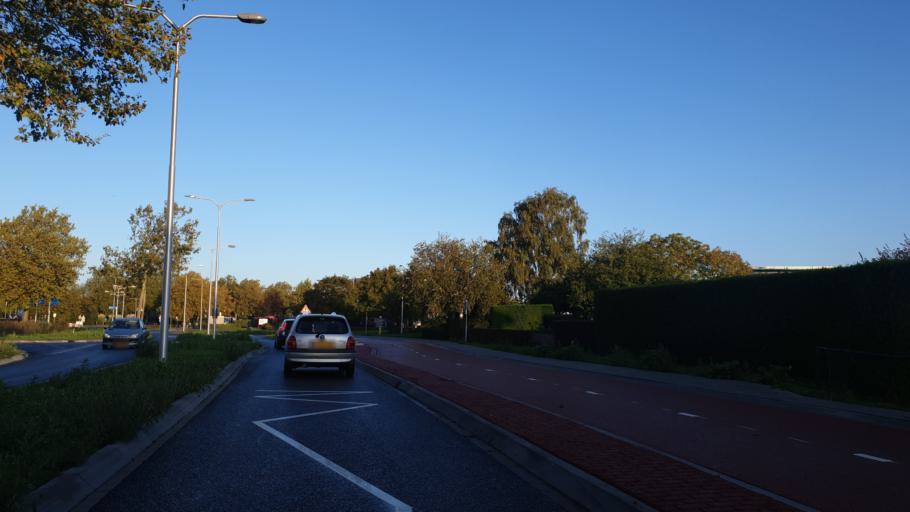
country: NL
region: Gelderland
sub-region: Gemeente Druten
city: Druten
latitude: 51.8835
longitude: 5.6079
